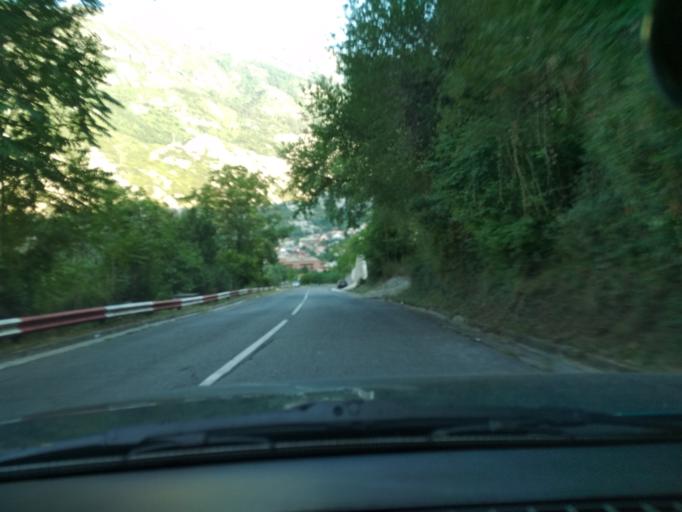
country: ME
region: Kotor
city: Kotor
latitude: 42.4190
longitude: 18.7599
